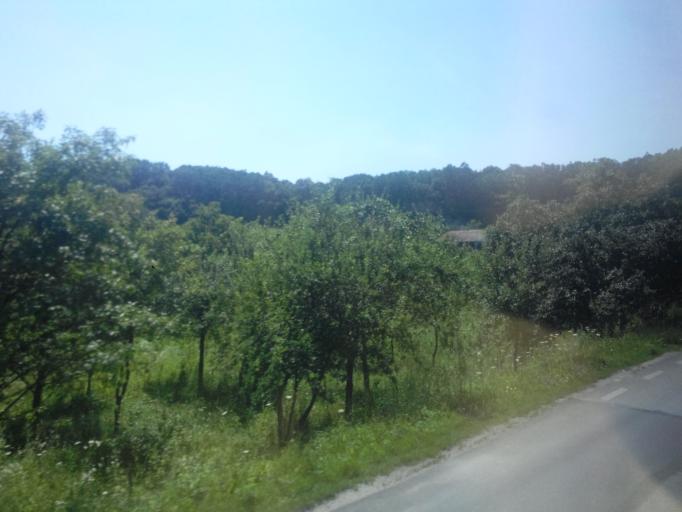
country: RO
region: Hunedoara
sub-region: Comuna Dobra
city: Dobra
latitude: 45.9099
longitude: 22.5331
